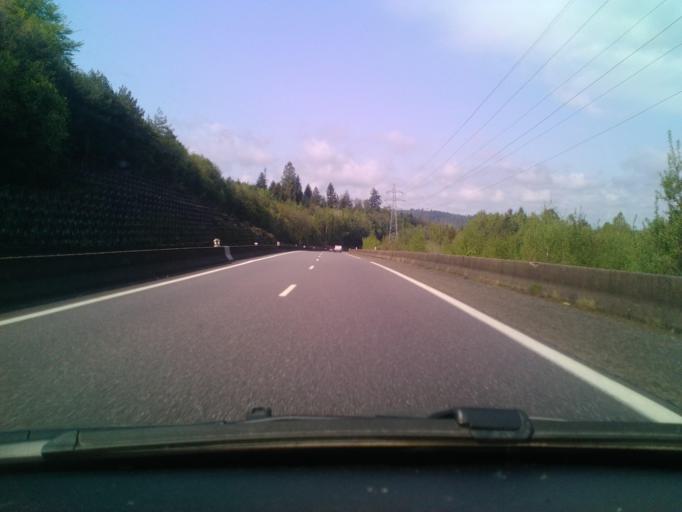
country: FR
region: Lorraine
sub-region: Departement des Vosges
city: Etival-Clairefontaine
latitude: 48.3967
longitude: 6.8412
